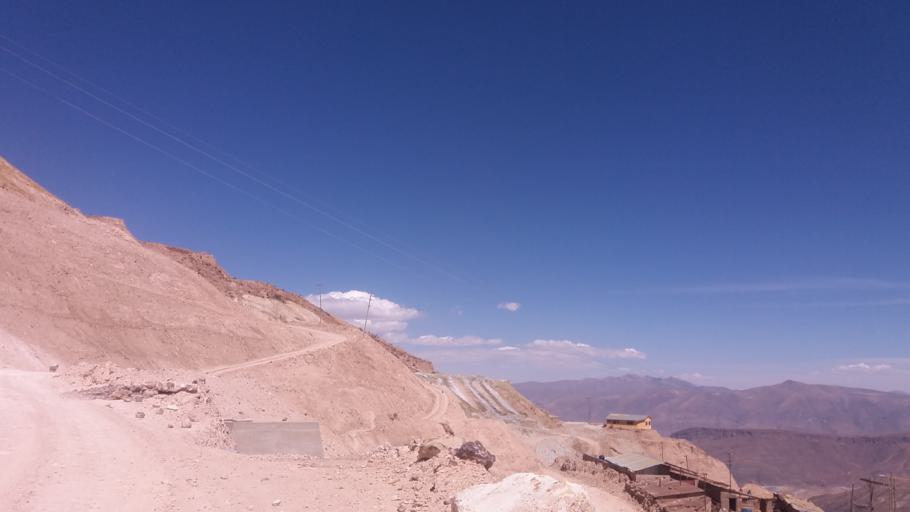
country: BO
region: Potosi
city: Potosi
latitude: -19.6123
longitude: -65.7464
